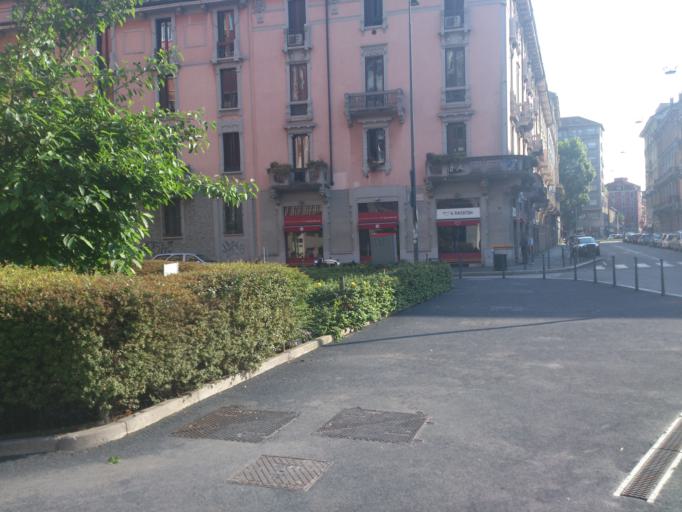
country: IT
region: Lombardy
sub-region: Citta metropolitana di Milano
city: Milano
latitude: 45.4519
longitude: 9.2057
